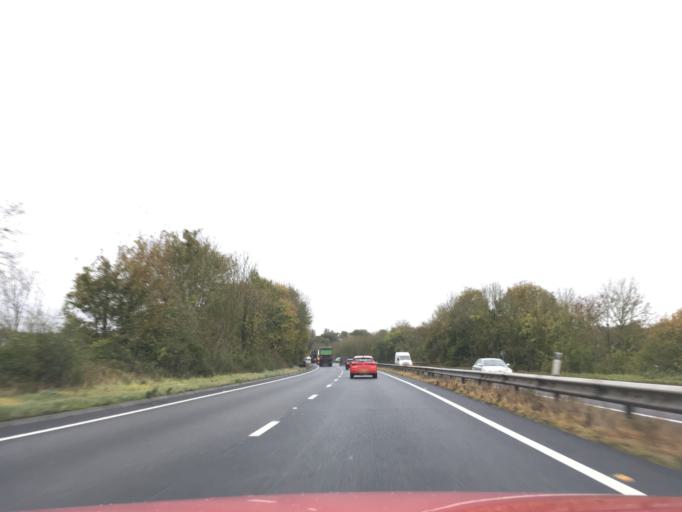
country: GB
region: England
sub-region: Hampshire
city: Overton
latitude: 51.2334
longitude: -1.3487
